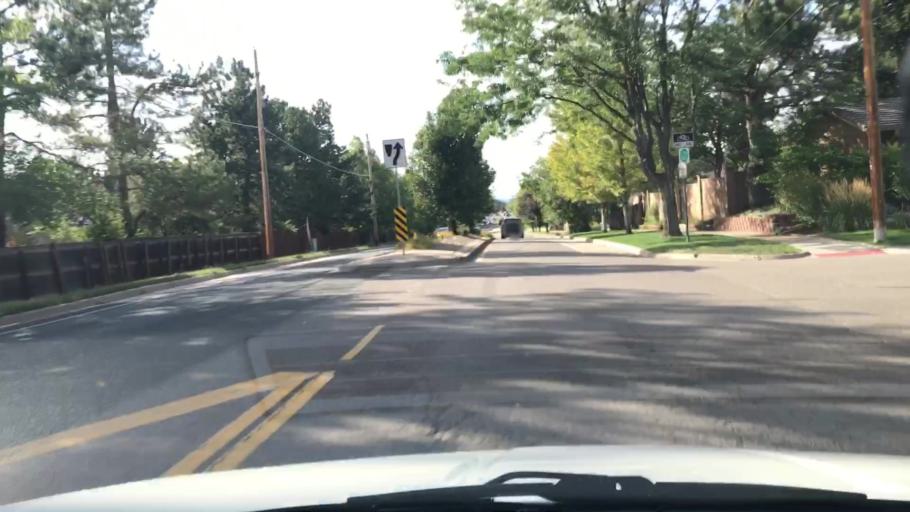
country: US
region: Colorado
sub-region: Arapahoe County
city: Cherry Hills Village
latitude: 39.6431
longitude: -104.9189
